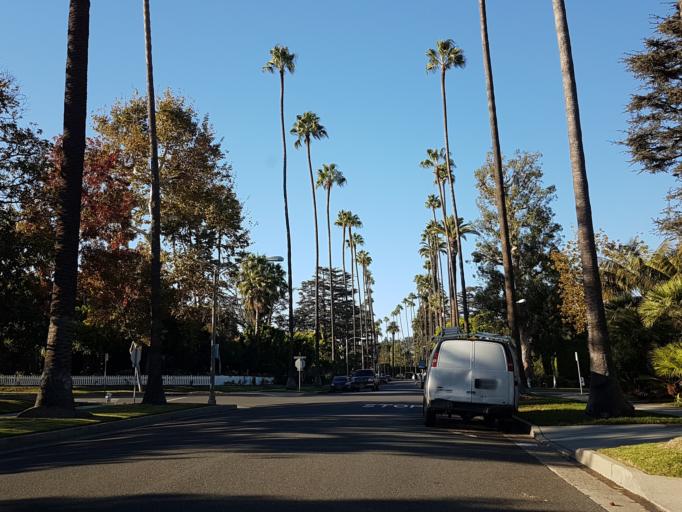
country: US
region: California
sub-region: Los Angeles County
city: Beverly Hills
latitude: 34.0776
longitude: -118.4004
